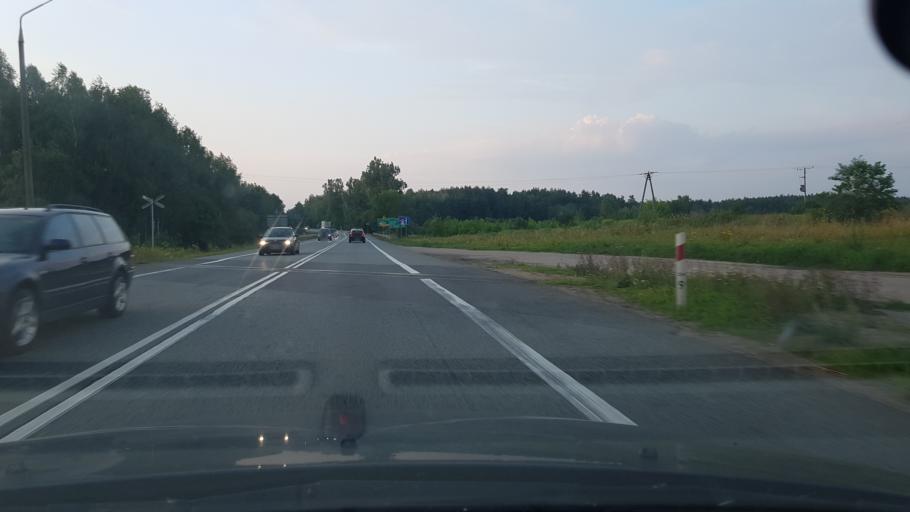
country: PL
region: Masovian Voivodeship
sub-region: Powiat mlawski
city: Mlawa
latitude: 53.1298
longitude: 20.3942
